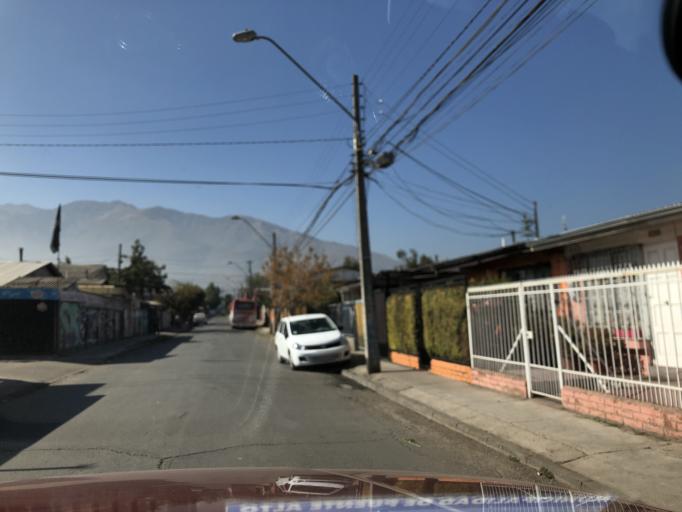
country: CL
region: Santiago Metropolitan
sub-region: Provincia de Cordillera
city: Puente Alto
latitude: -33.5644
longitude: -70.5697
